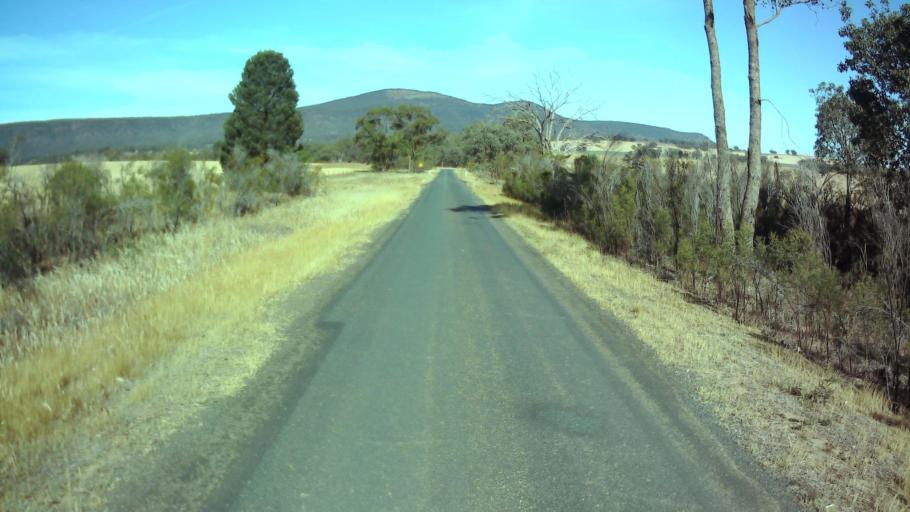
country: AU
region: New South Wales
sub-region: Weddin
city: Grenfell
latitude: -33.9037
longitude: 148.0469
